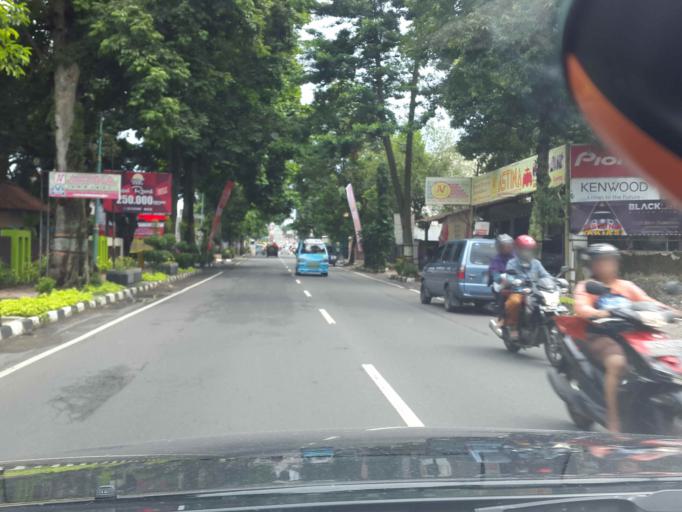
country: ID
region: Central Java
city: Salatiga
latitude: -7.3409
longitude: 110.5091
